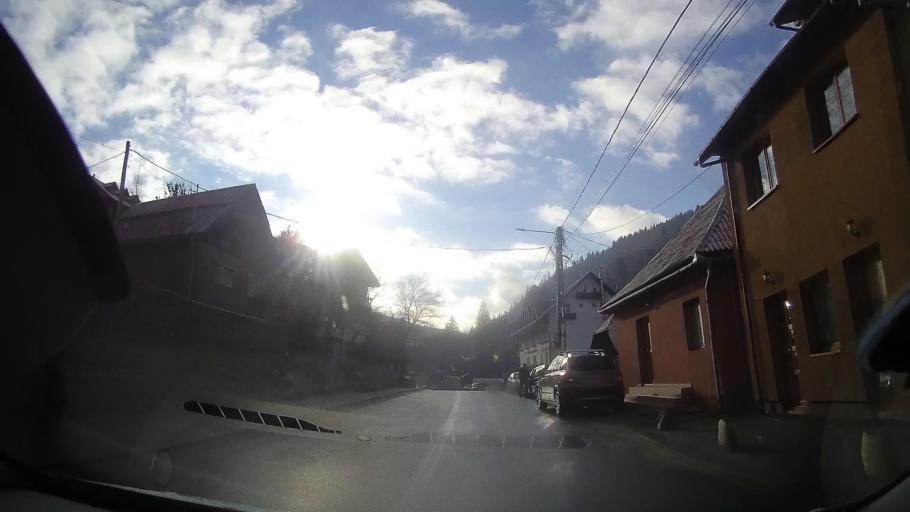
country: RO
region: Alba
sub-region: Comuna Albac
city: Albac
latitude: 46.4468
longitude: 22.9643
